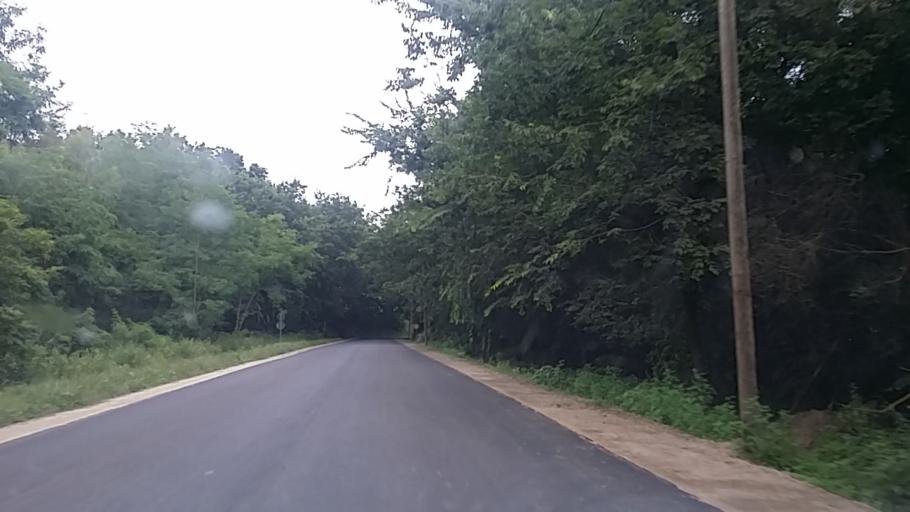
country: HU
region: Tolna
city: Tengelic
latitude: 46.5464
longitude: 18.6885
